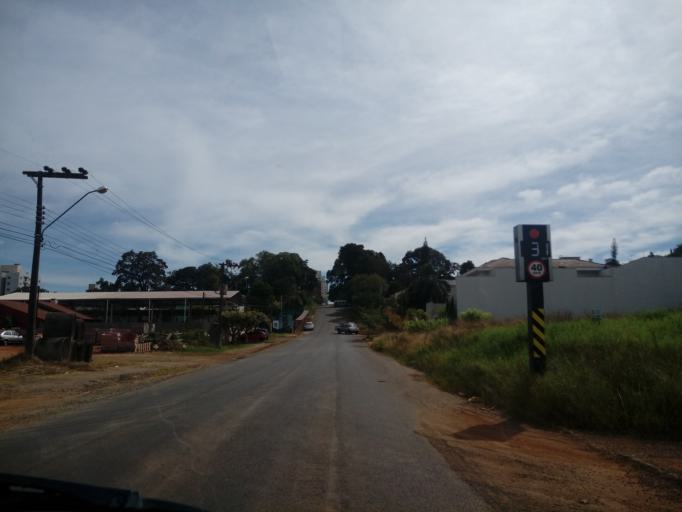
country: BR
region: Santa Catarina
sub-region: Chapeco
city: Chapeco
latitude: -27.1168
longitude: -52.6146
